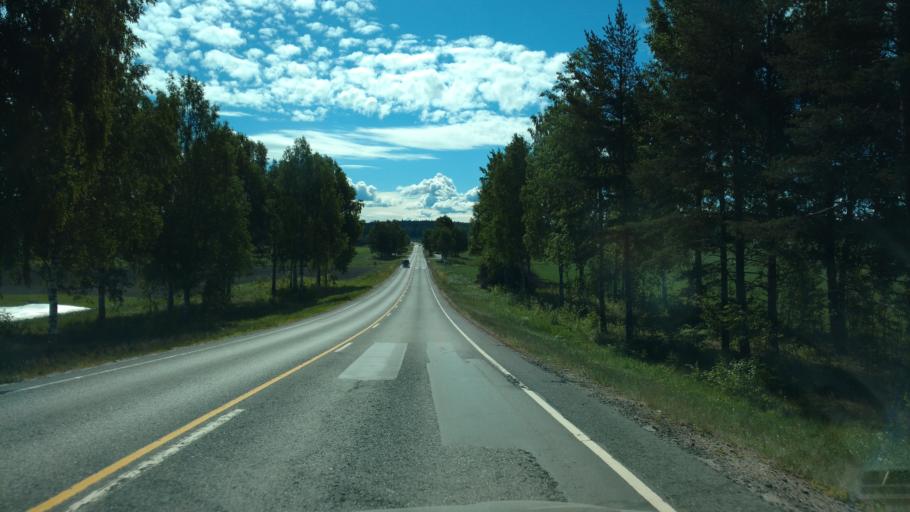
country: FI
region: Varsinais-Suomi
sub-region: Salo
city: Muurla
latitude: 60.3800
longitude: 23.2988
